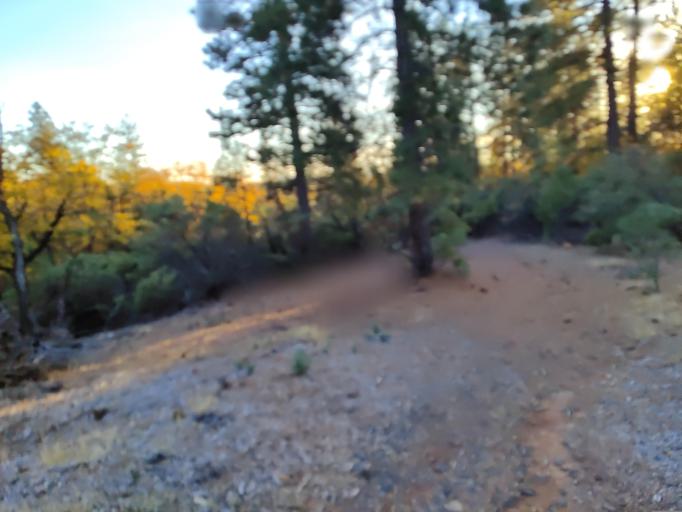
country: US
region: California
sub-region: Placer County
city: Meadow Vista
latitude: 39.0355
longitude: -120.9834
